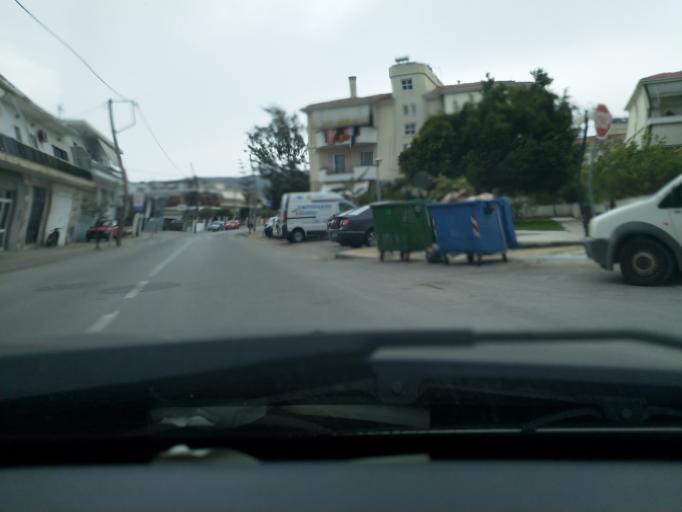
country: GR
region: Crete
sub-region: Nomos Chanias
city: Chania
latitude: 35.4963
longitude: 24.0221
